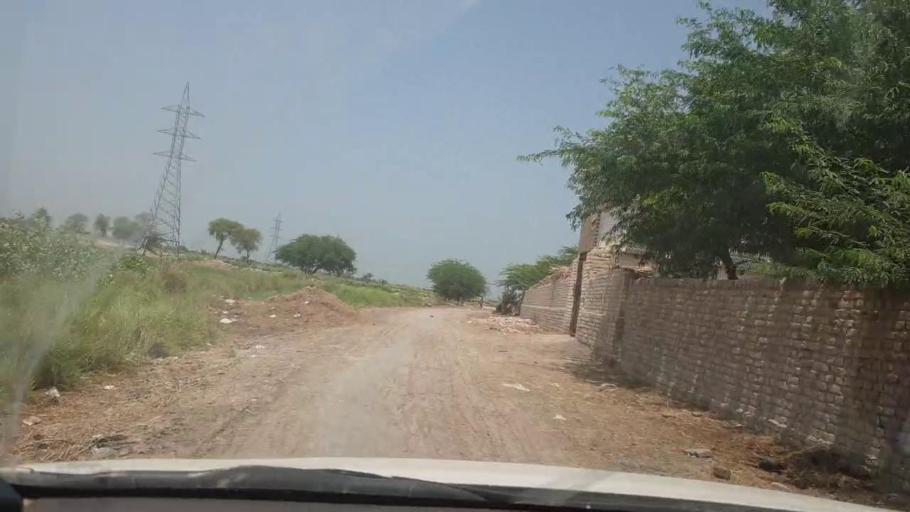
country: PK
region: Sindh
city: Lakhi
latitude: 27.8666
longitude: 68.6977
